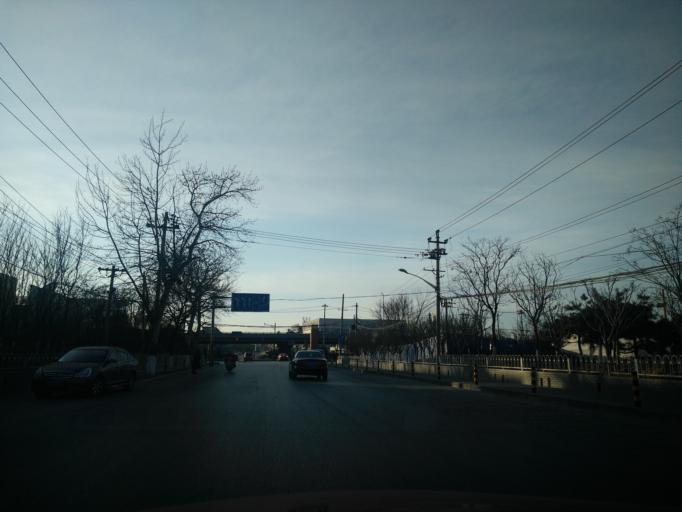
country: CN
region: Beijing
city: Huaxiang
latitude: 39.8208
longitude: 116.3408
